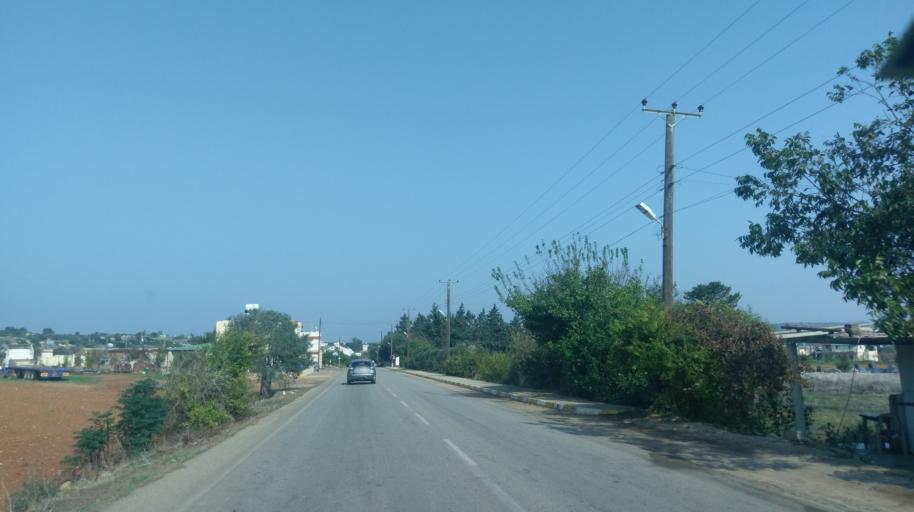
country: CY
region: Ammochostos
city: Leonarisso
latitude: 35.4950
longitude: 34.1575
